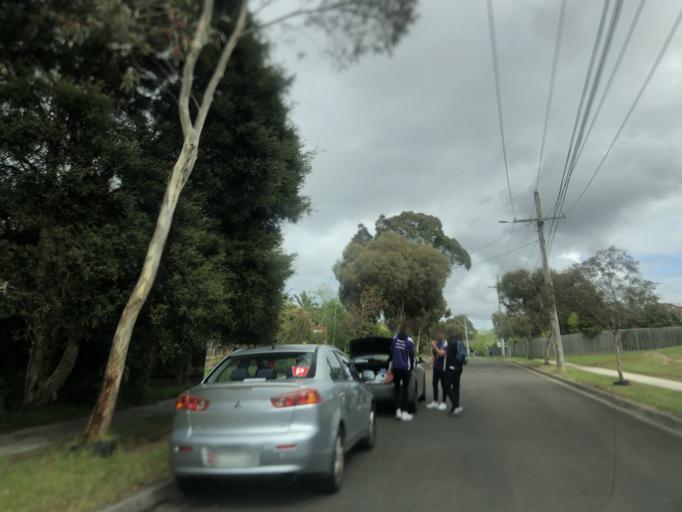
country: AU
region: Victoria
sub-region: Knox
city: Rowville
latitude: -37.9389
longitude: 145.2275
